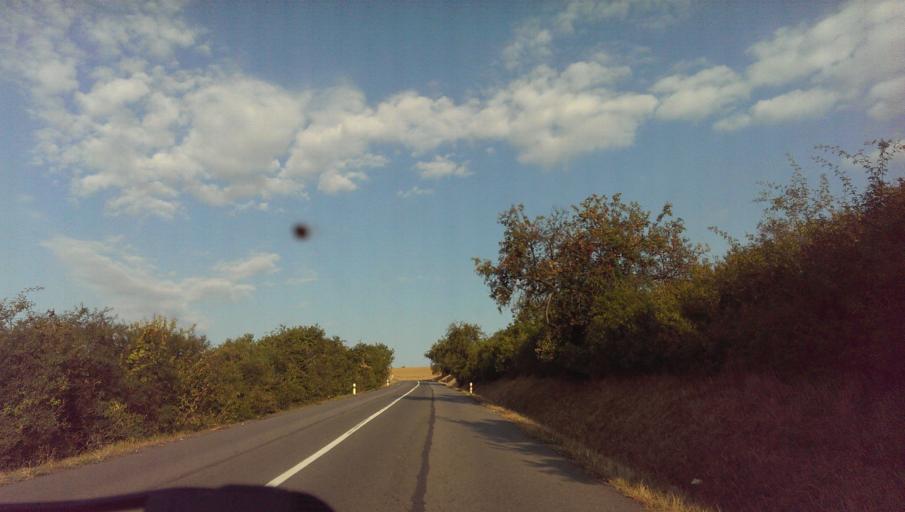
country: CZ
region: South Moravian
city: Domanin
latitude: 49.0527
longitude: 17.2838
